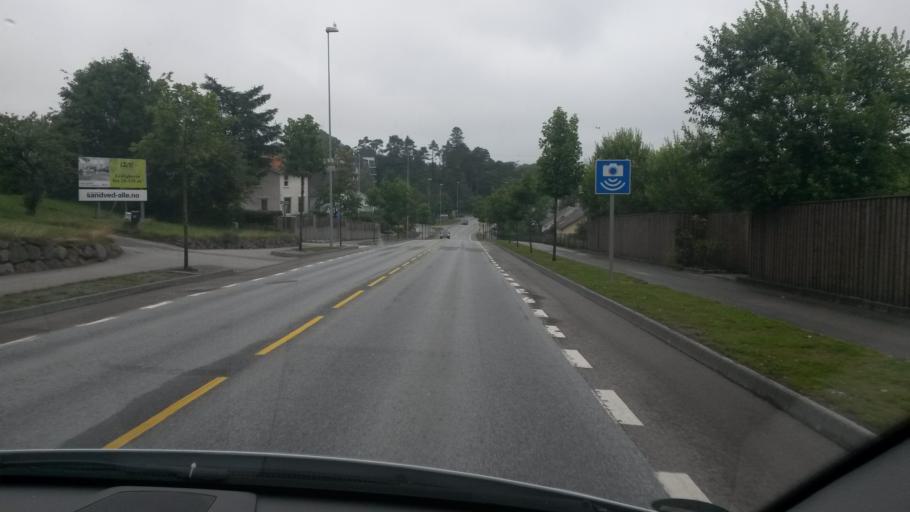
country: NO
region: Rogaland
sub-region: Sandnes
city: Sandnes
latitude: 58.8316
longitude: 5.7182
